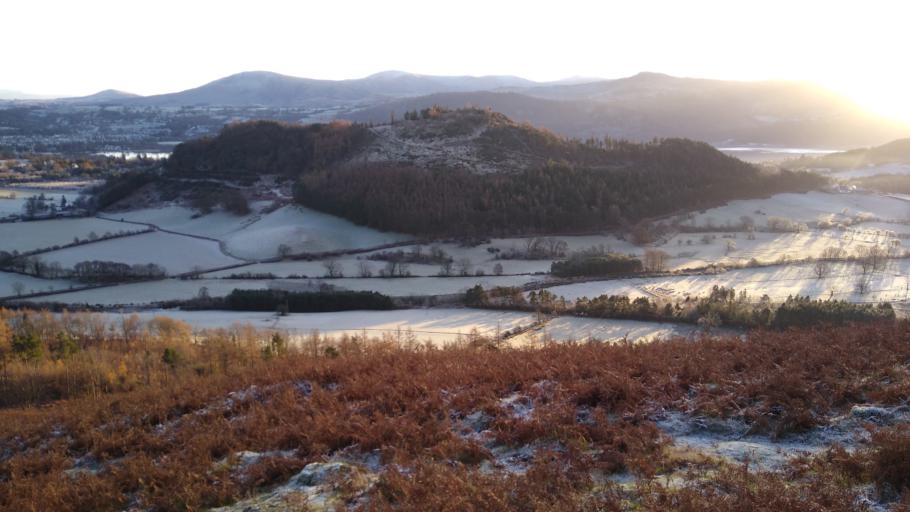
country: GB
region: England
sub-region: Cumbria
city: Keswick
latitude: 54.5945
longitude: -3.1893
